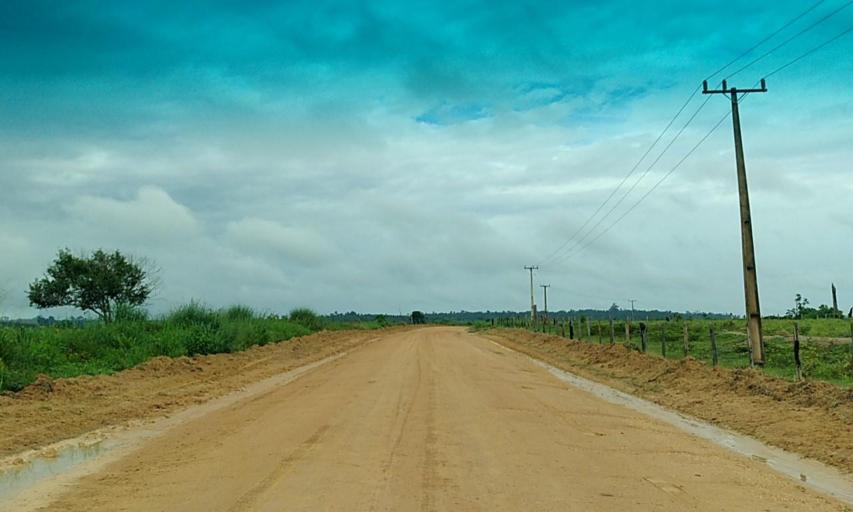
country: BR
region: Para
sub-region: Senador Jose Porfirio
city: Senador Jose Porfirio
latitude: -3.0376
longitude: -51.6803
